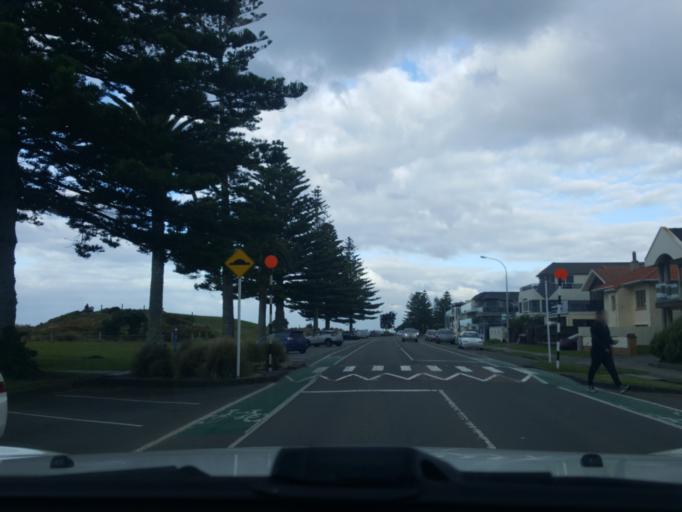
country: NZ
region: Bay of Plenty
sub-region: Tauranga City
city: Tauranga
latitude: -37.6353
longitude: 176.1860
